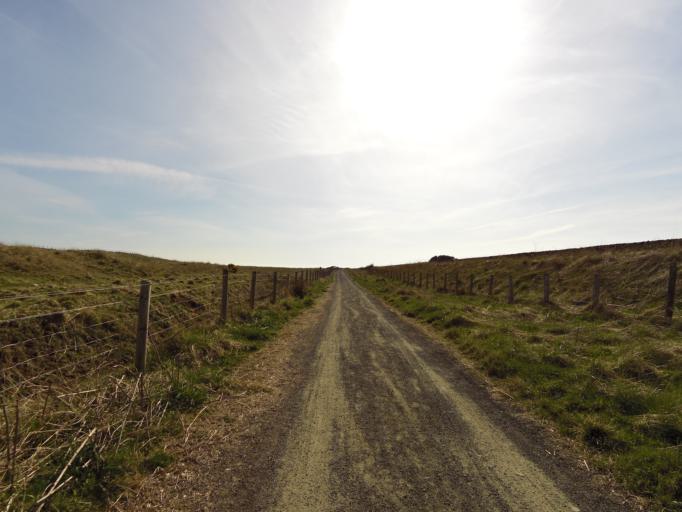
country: GB
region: Scotland
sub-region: Angus
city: Arbroath
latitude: 56.5315
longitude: -2.6343
